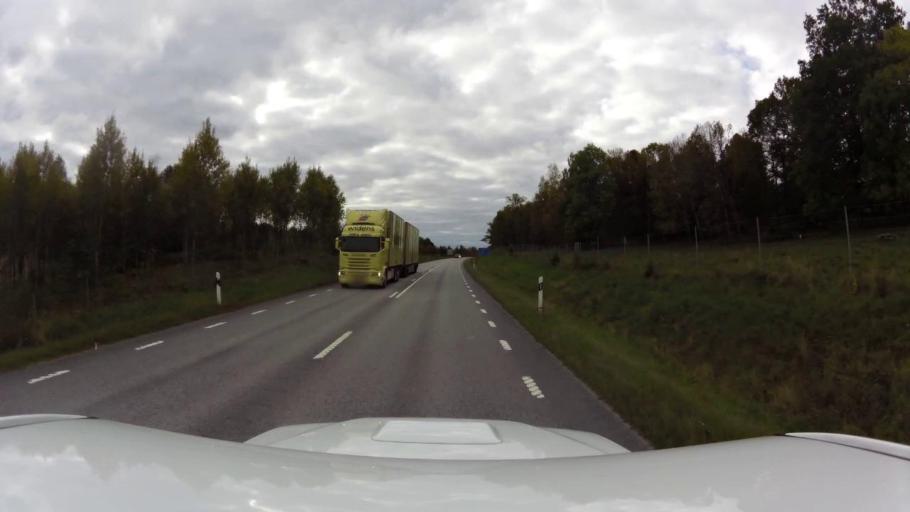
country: SE
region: OEstergoetland
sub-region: Kinda Kommun
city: Rimforsa
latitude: 58.2091
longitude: 15.6688
